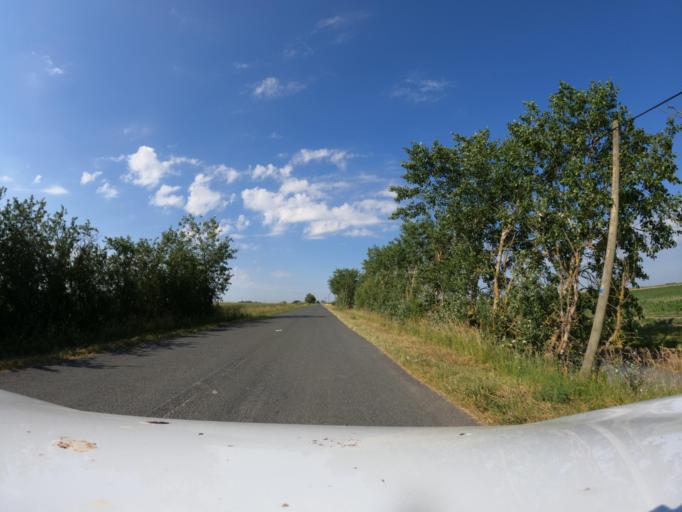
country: FR
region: Pays de la Loire
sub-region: Departement de la Vendee
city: Champagne-les-Marais
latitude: 46.3655
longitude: -1.1093
